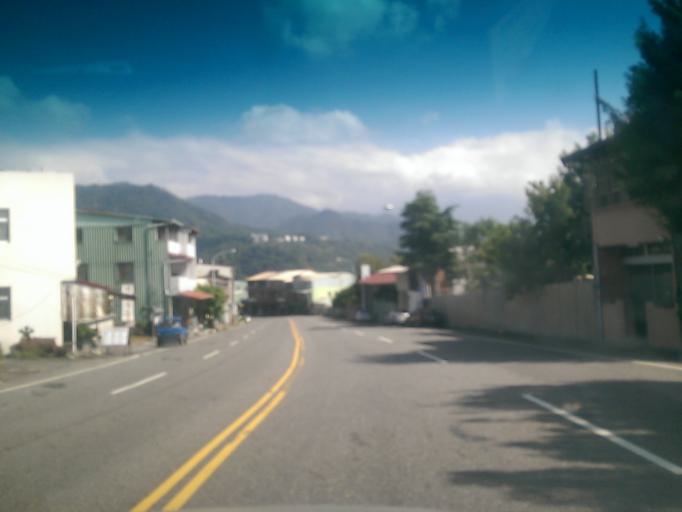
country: TW
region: Taiwan
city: Lugu
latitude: 23.8193
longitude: 120.8449
